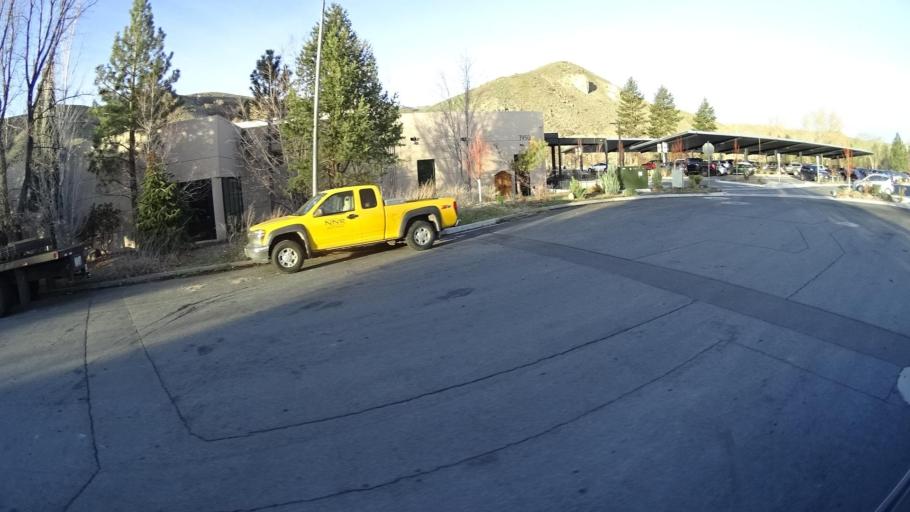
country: US
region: Nevada
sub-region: Washoe County
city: Mogul
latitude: 39.5046
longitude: -119.8983
